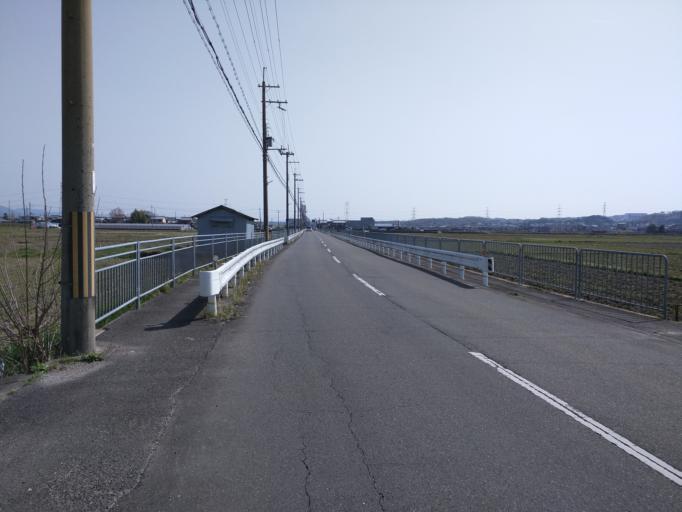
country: JP
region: Kyoto
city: Tanabe
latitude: 34.7716
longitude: 135.7975
